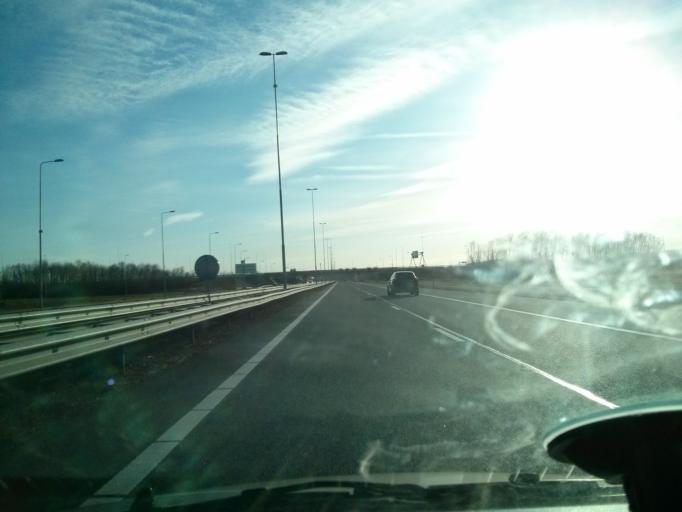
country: NL
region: Gelderland
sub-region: Gemeente Wijchen
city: Bergharen
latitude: 51.8606
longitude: 5.7143
